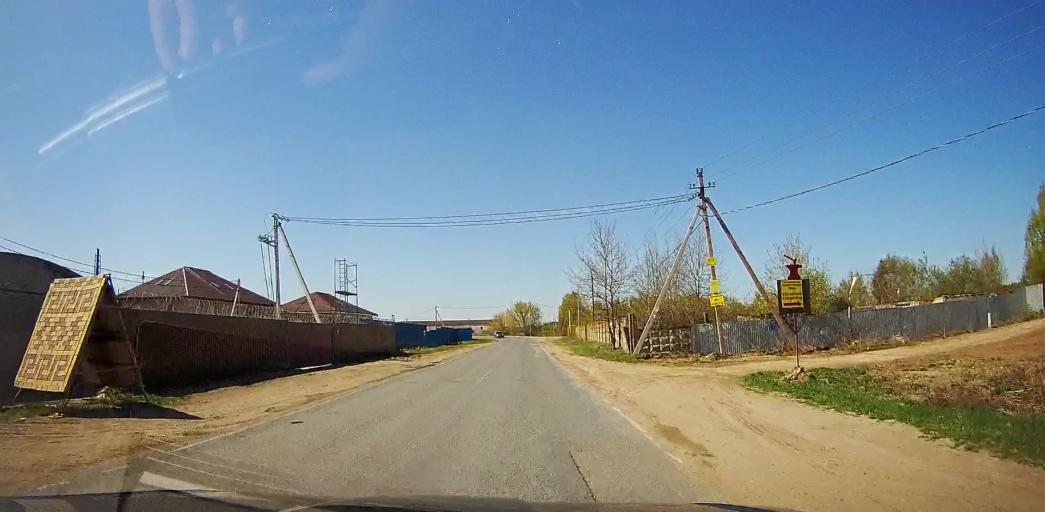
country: RU
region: Moskovskaya
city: Malyshevo
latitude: 55.4577
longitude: 38.3084
